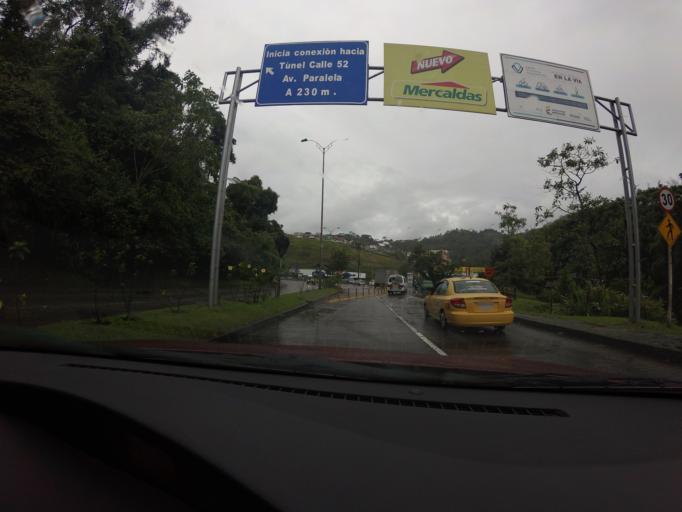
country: CO
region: Caldas
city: Manizales
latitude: 5.0624
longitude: -75.4855
